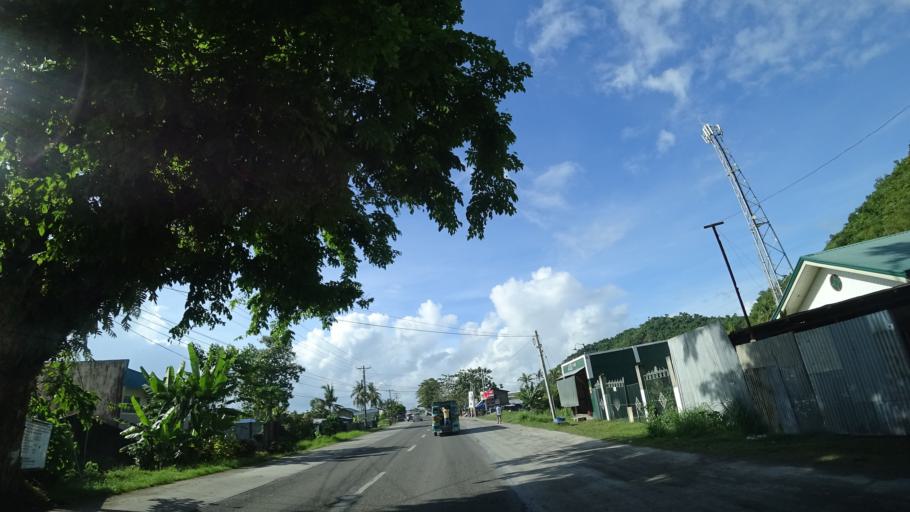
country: PH
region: Eastern Visayas
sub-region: Province of Leyte
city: Pawing
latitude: 11.1953
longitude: 124.9917
